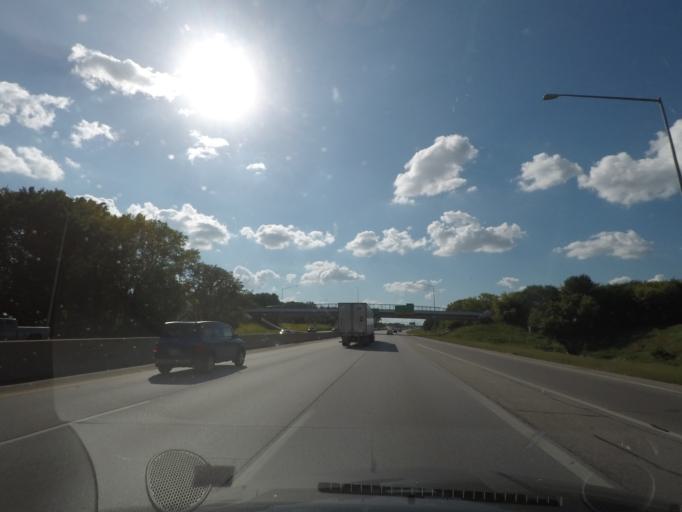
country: US
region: Iowa
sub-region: Polk County
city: Clive
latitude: 41.5928
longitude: -93.7407
